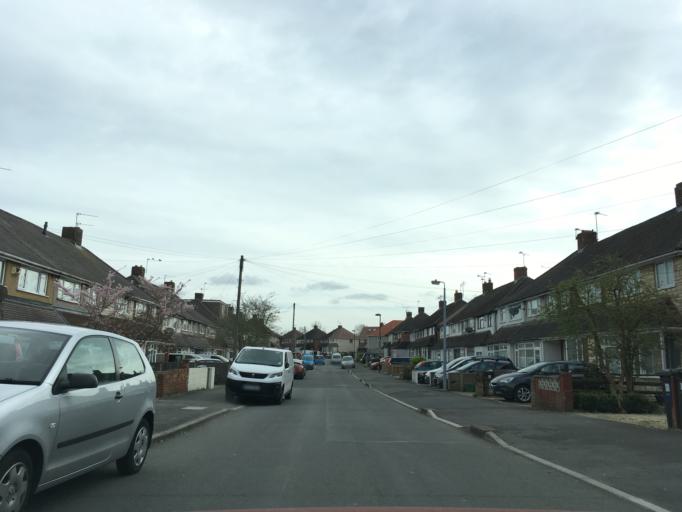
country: GB
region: England
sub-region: South Gloucestershire
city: Almondsbury
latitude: 51.5336
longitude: -2.5849
